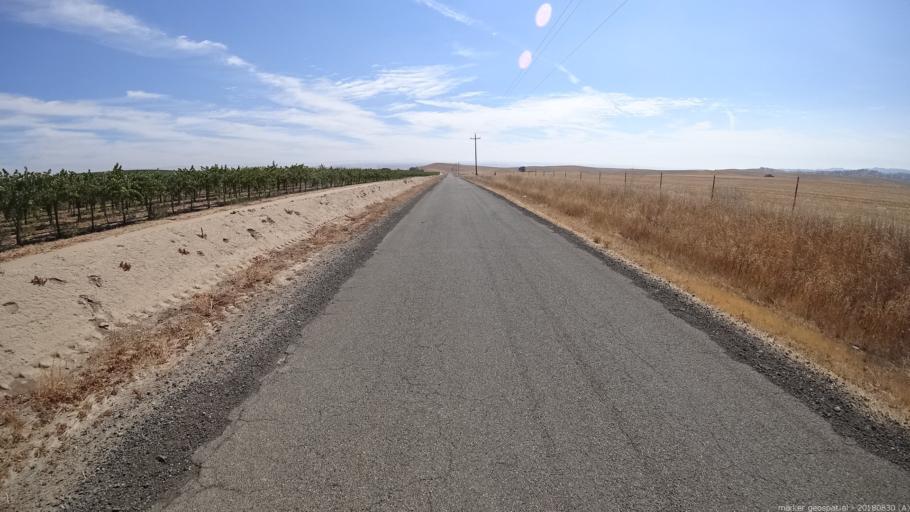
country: US
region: California
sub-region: Monterey County
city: King City
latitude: 36.1109
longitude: -121.0784
